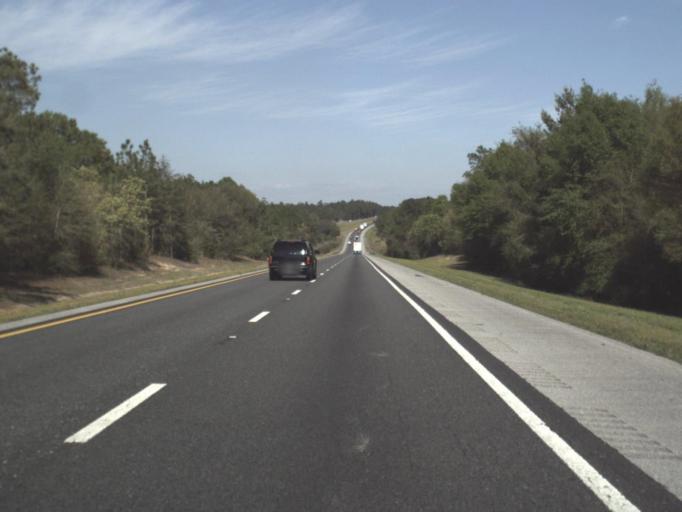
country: US
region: Florida
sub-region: Okaloosa County
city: Crestview
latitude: 30.7122
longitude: -86.7014
